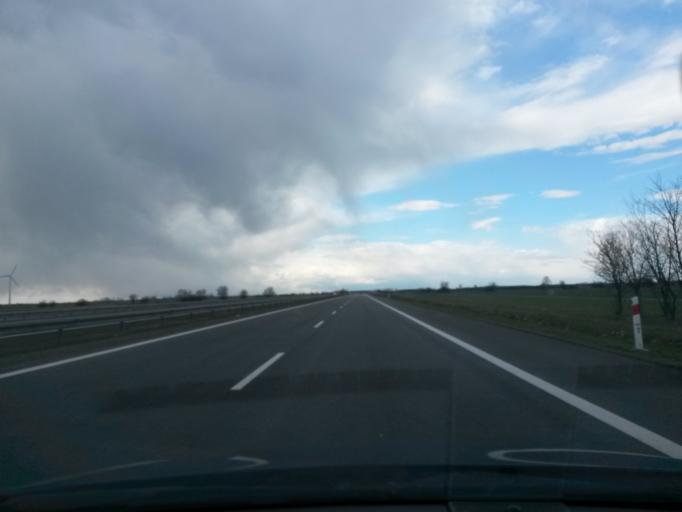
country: PL
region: Greater Poland Voivodeship
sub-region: Powiat koninski
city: Rzgow Pierwszy
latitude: 52.2080
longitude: 18.0086
